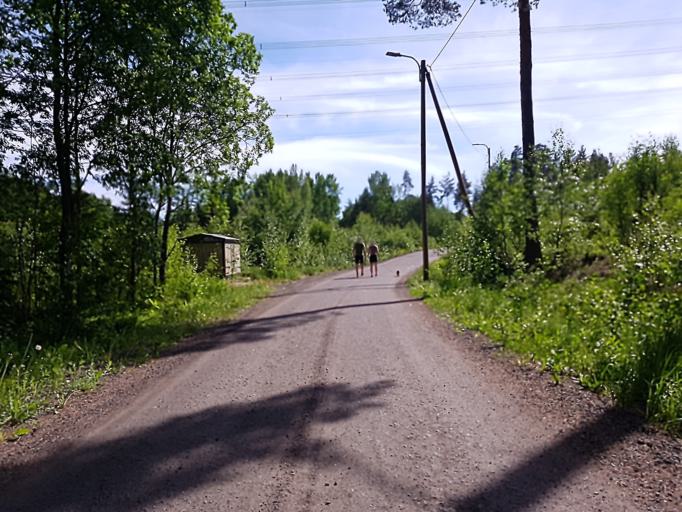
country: FI
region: Uusimaa
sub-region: Helsinki
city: Helsinki
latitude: 60.2914
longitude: 24.9165
